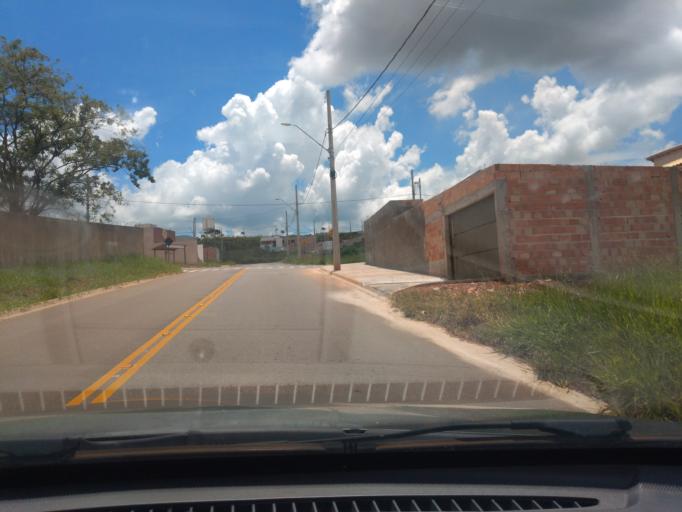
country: BR
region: Minas Gerais
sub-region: Tres Coracoes
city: Tres Coracoes
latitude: -21.6809
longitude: -45.2751
